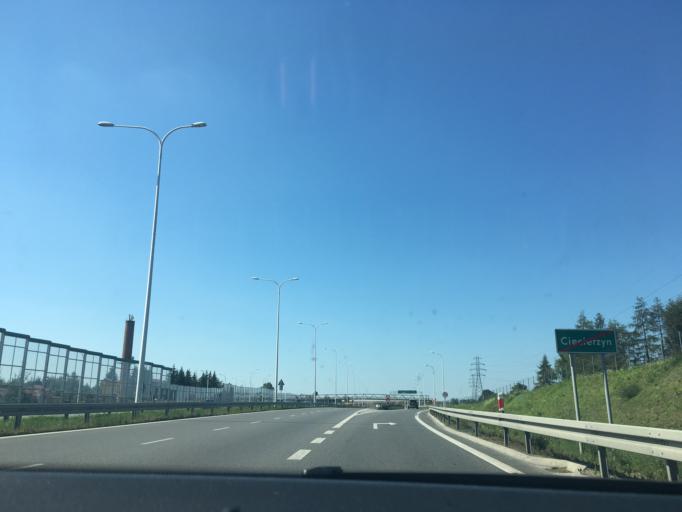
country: PL
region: Lublin Voivodeship
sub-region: Powiat lubelski
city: Jakubowice Murowane
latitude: 51.3079
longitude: 22.5940
